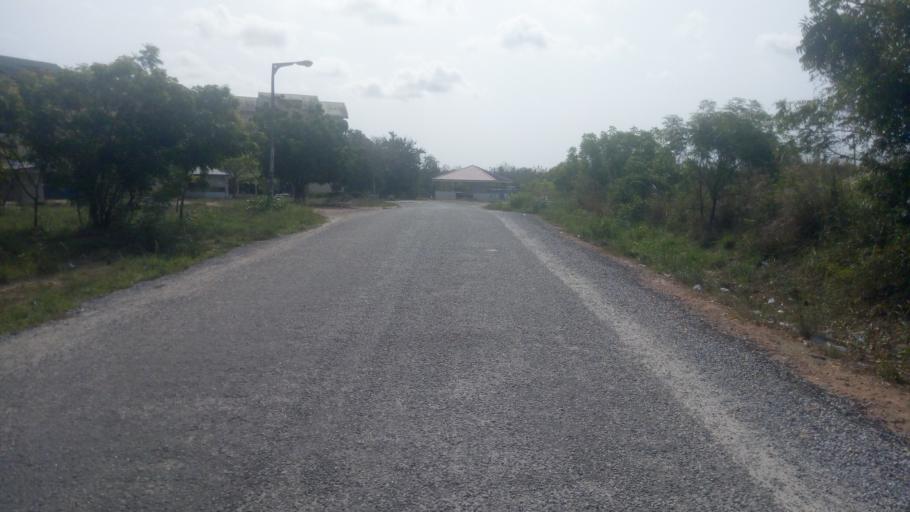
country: GH
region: Central
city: Winneba
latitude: 5.3791
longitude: -0.6226
